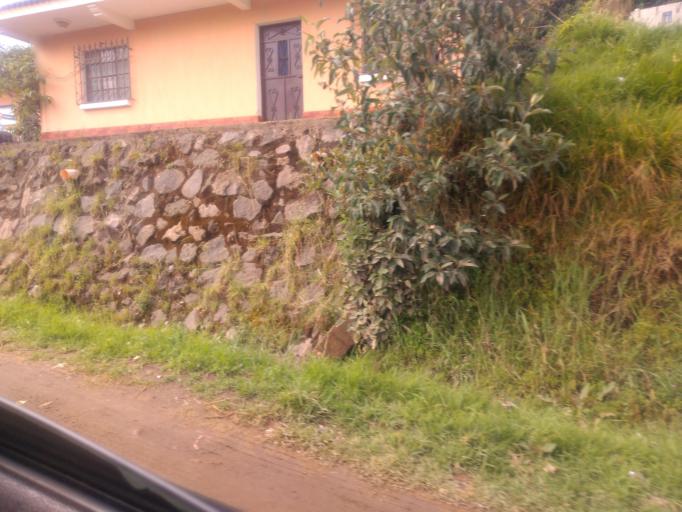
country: GT
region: Quetzaltenango
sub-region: Municipio de La Esperanza
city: La Esperanza
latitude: 14.8573
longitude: -91.5720
